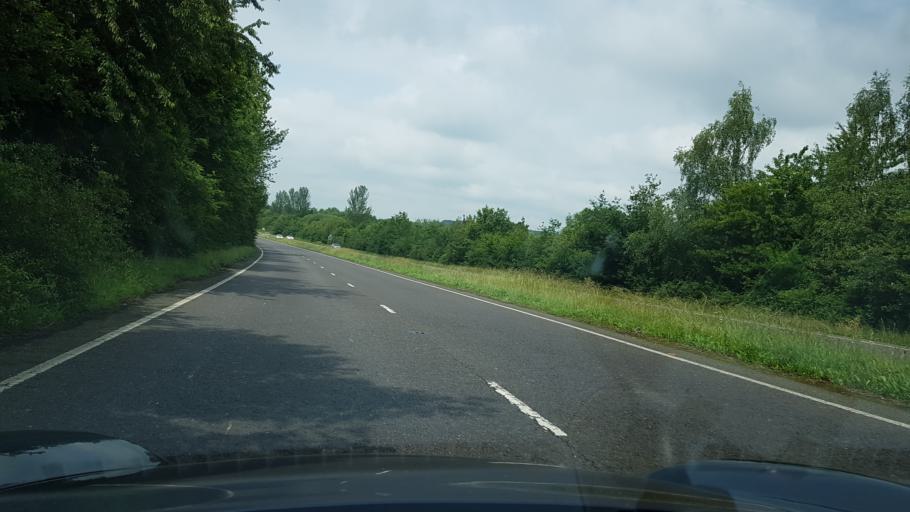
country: GB
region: England
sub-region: West Sussex
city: Horsham
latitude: 51.0862
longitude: -0.2951
